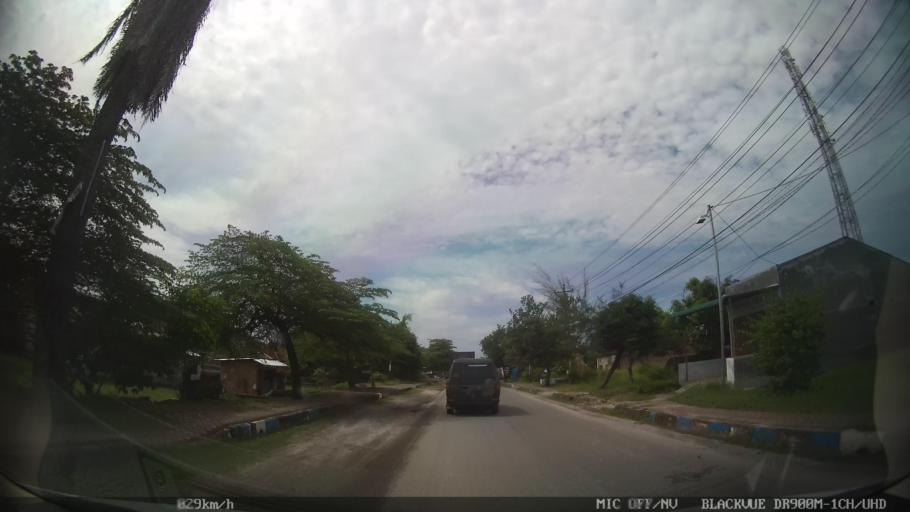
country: ID
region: North Sumatra
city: Percut
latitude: 3.6007
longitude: 98.8075
